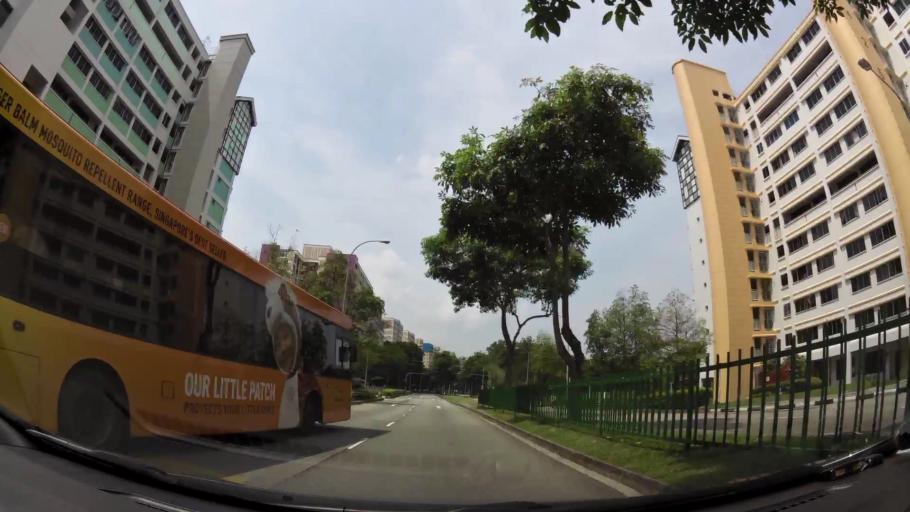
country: MY
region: Johor
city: Kampung Pasir Gudang Baru
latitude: 1.3693
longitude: 103.9551
